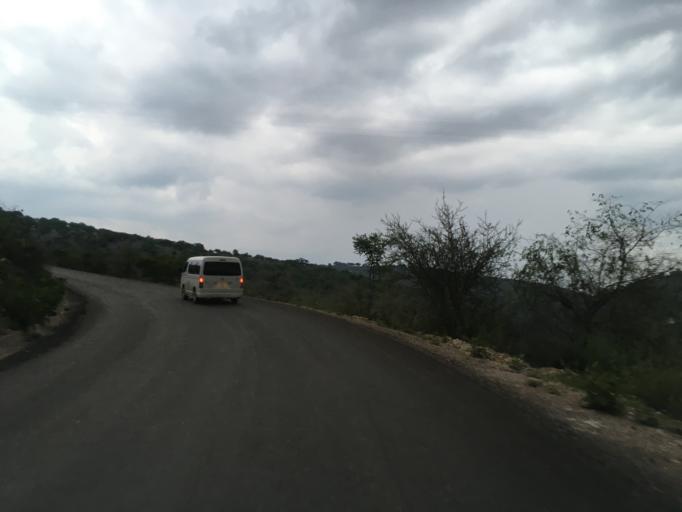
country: MX
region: Oaxaca
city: Magdalena Jaltepec
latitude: 17.2965
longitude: -97.2736
